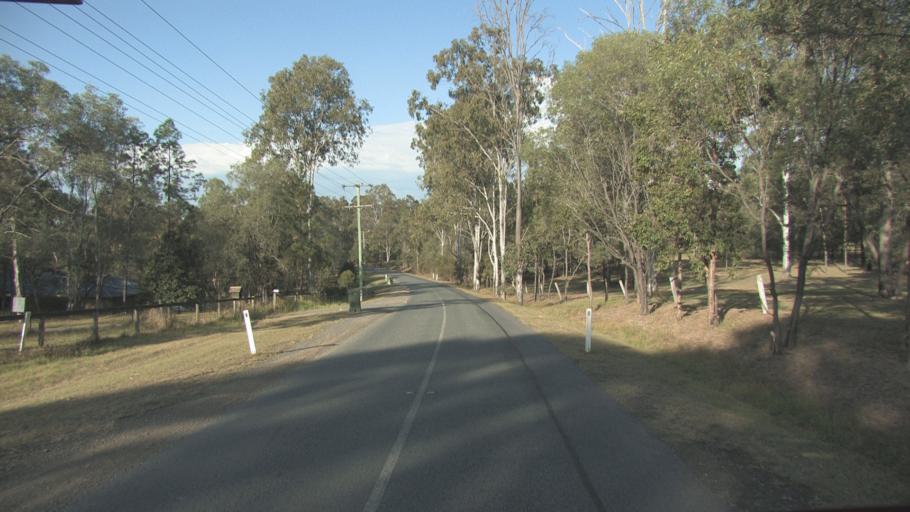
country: AU
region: Queensland
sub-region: Logan
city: Cedar Vale
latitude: -27.8483
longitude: 153.0981
